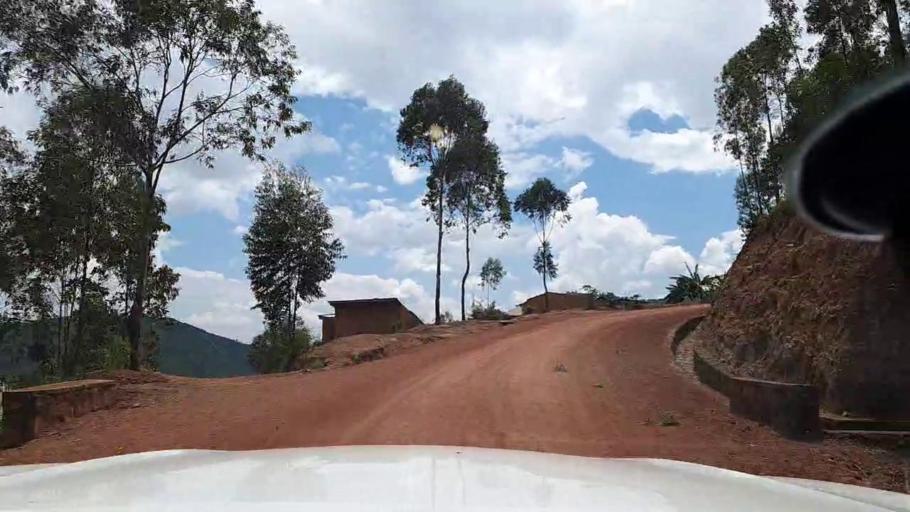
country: RW
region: Northern Province
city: Byumba
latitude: -1.7558
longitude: 29.8507
